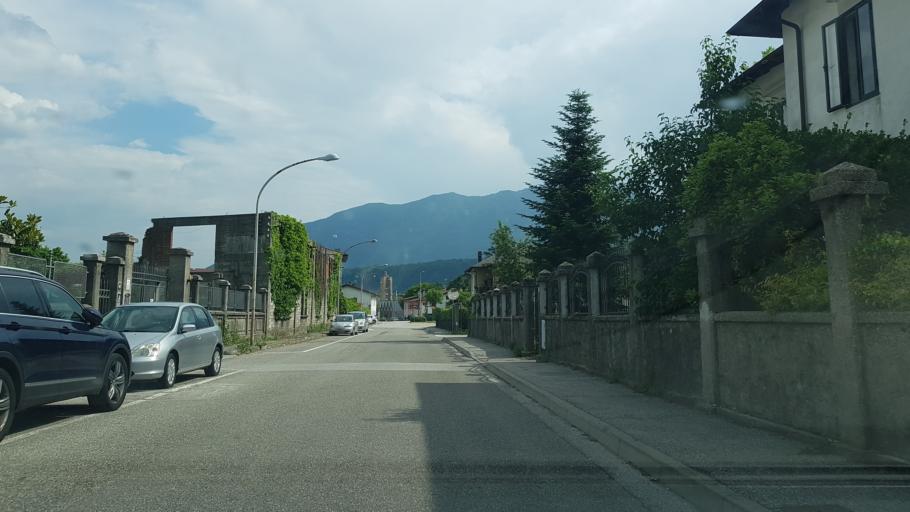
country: IT
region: Friuli Venezia Giulia
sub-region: Provincia di Udine
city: Tolmezzo
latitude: 46.4009
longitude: 13.0178
